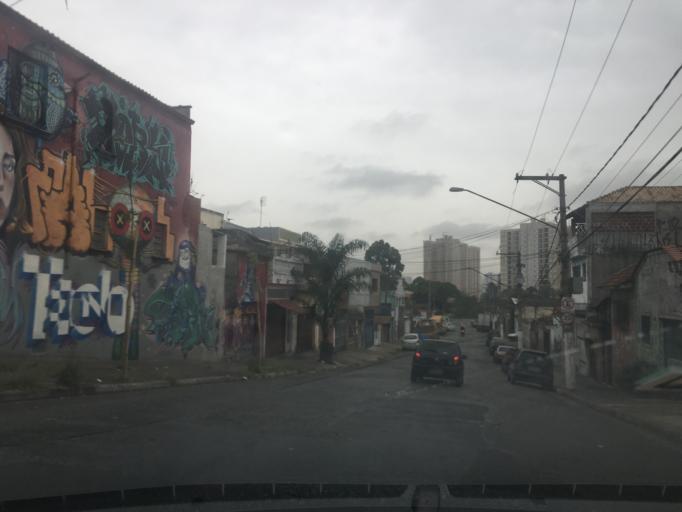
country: BR
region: Sao Paulo
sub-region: Guarulhos
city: Guarulhos
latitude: -23.5178
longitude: -46.5495
